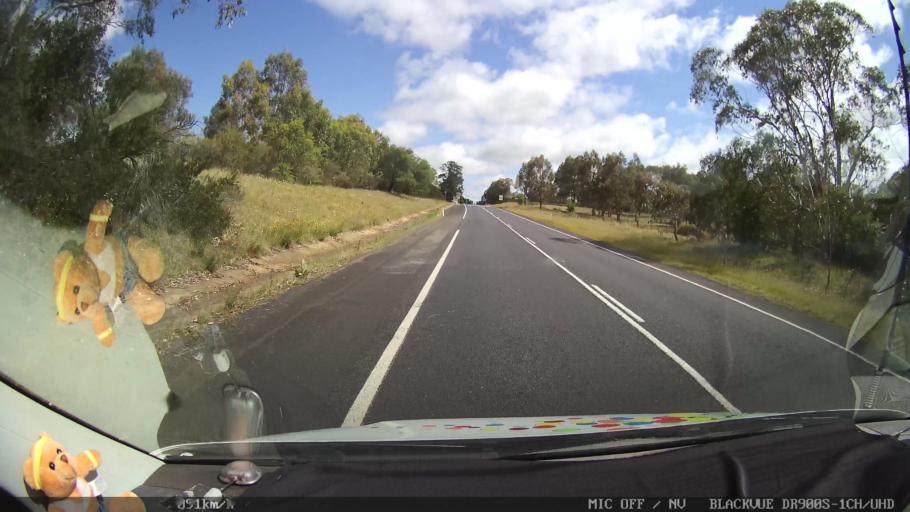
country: AU
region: New South Wales
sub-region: Glen Innes Severn
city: Glen Innes
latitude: -29.9341
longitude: 151.7240
